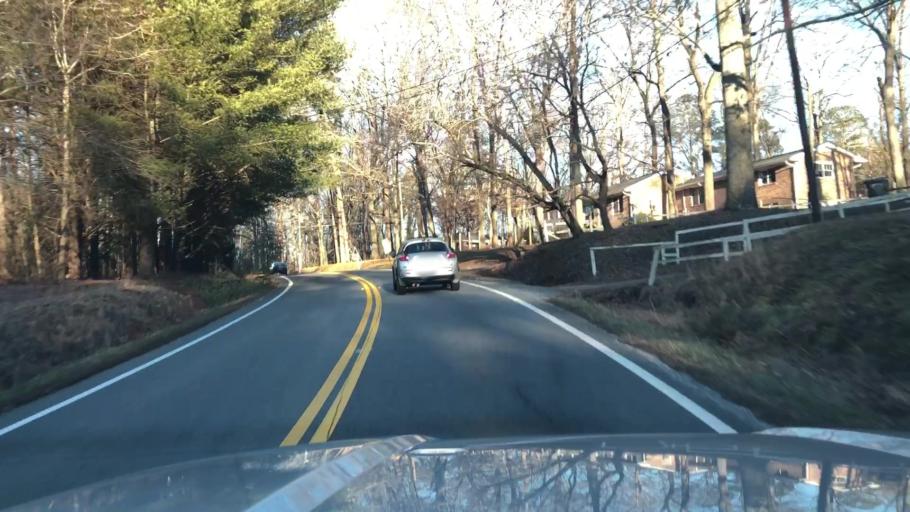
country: US
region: Georgia
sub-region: Cherokee County
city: Canton
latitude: 34.2107
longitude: -84.5130
